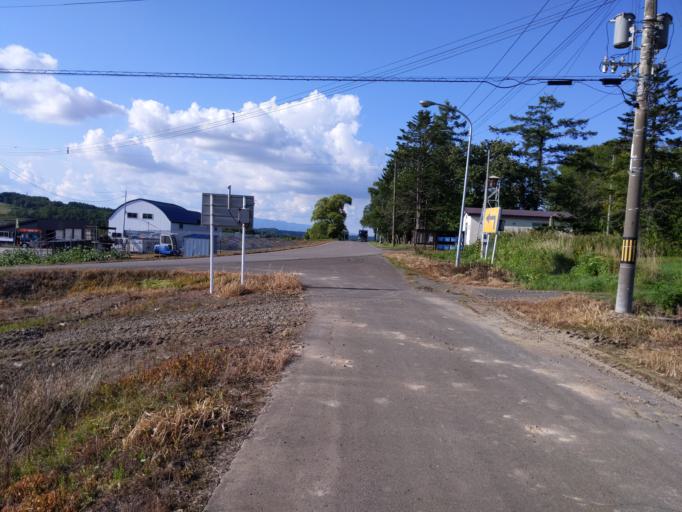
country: JP
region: Hokkaido
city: Iwamizawa
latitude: 43.1989
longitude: 141.8287
